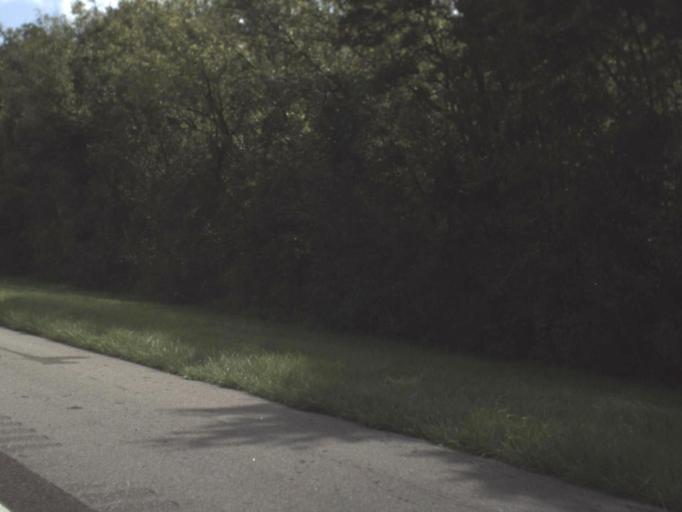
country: US
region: Florida
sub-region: Hillsborough County
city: Lutz
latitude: 28.1309
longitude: -82.4153
